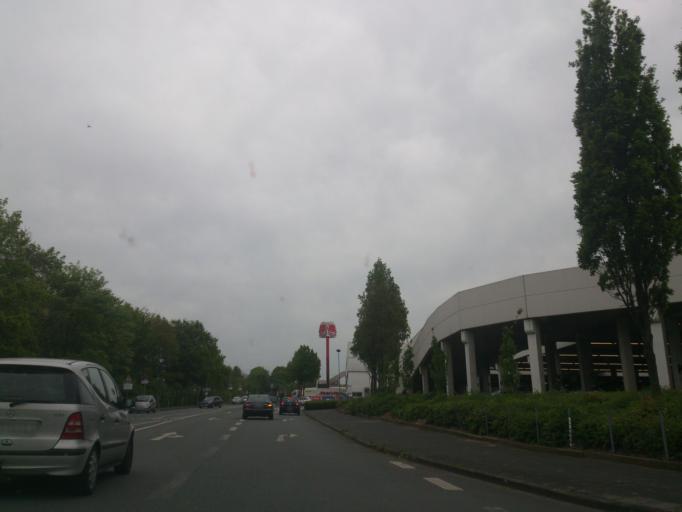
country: DE
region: North Rhine-Westphalia
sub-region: Regierungsbezirk Detmold
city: Paderborn
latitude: 51.7053
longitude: 8.7705
